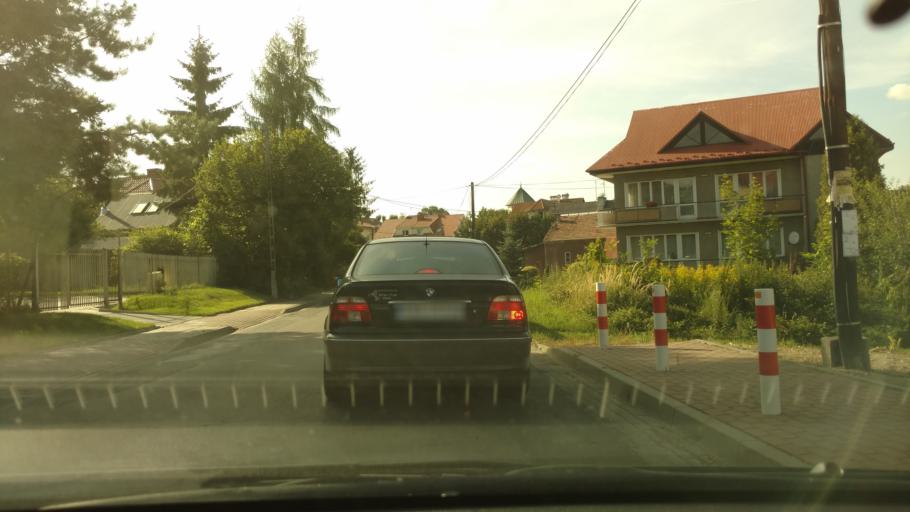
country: PL
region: Lesser Poland Voivodeship
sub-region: Powiat krakowski
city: Michalowice
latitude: 50.1161
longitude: 19.9709
